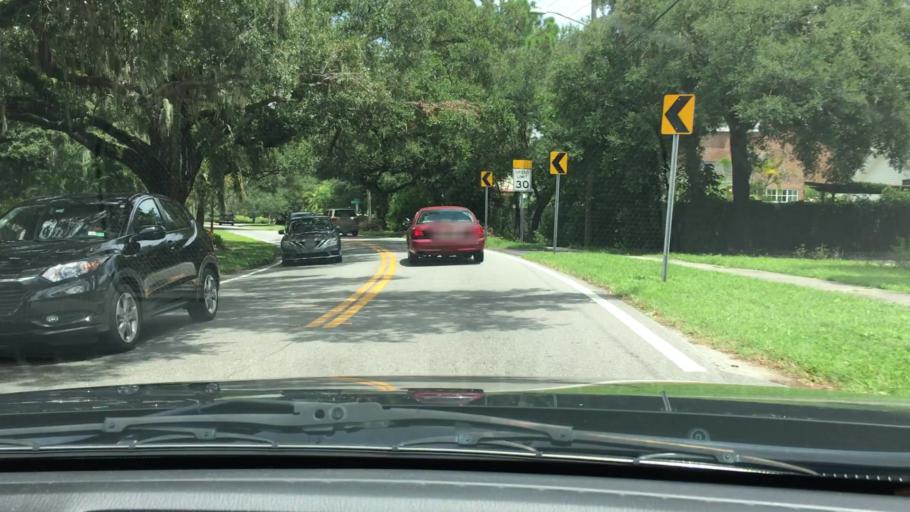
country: US
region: Florida
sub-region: Hillsborough County
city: Tampa
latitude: 27.9196
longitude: -82.5234
